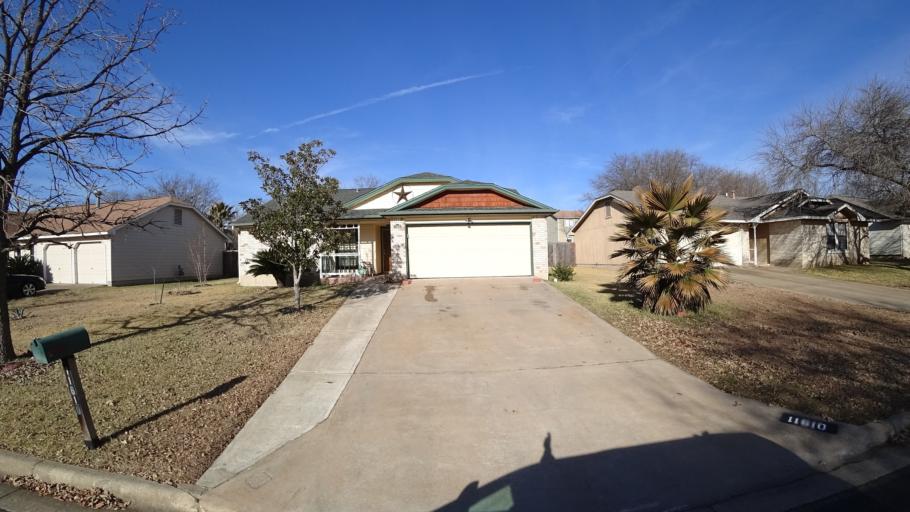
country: US
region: Texas
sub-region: Travis County
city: Wells Branch
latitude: 30.3926
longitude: -97.6995
